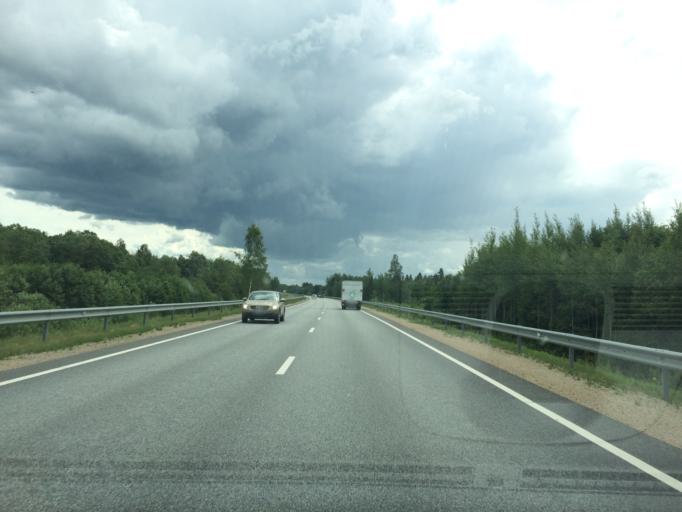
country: LV
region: Skriveri
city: Skriveri
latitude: 56.7387
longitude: 25.1379
